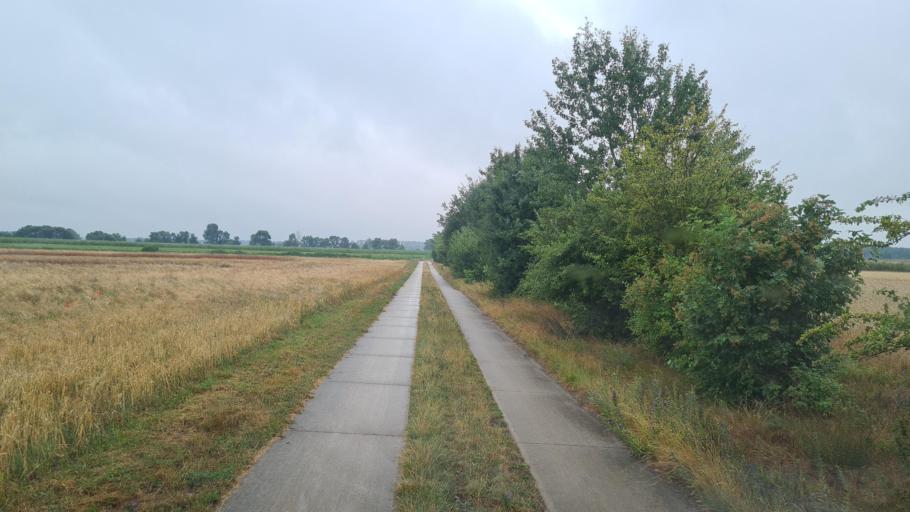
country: DE
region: Brandenburg
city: Trebbin
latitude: 52.1880
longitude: 13.2587
